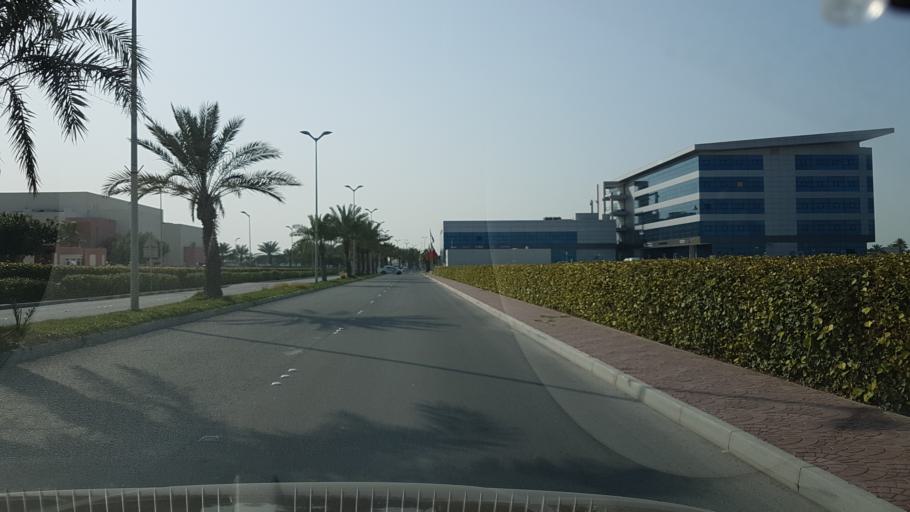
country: BH
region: Muharraq
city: Al Hadd
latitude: 26.2782
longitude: 50.6667
